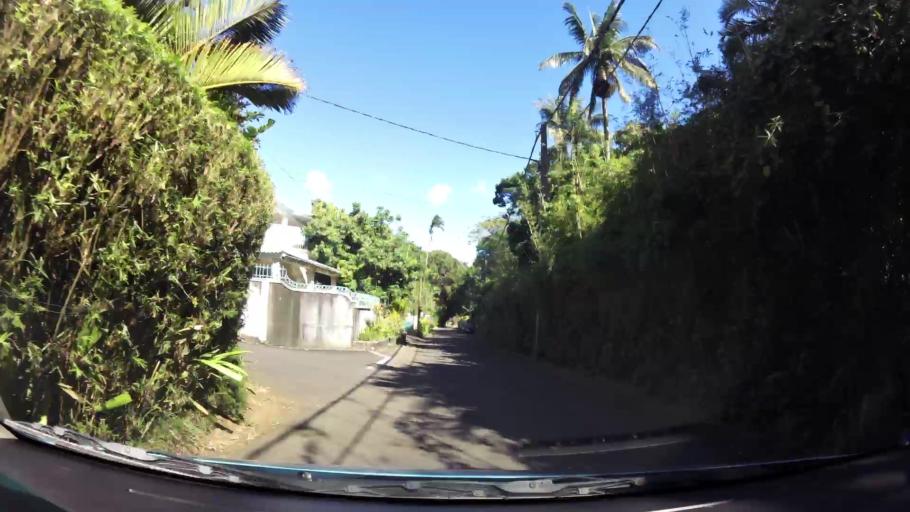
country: MU
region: Plaines Wilhems
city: Vacoas
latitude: -20.2987
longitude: 57.4955
